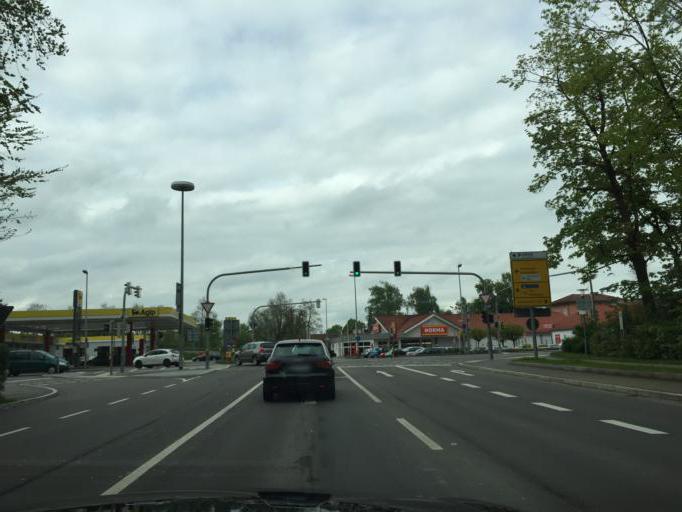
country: DE
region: Bavaria
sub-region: Swabia
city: Dillingen an der Donau
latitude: 48.5794
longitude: 10.4885
